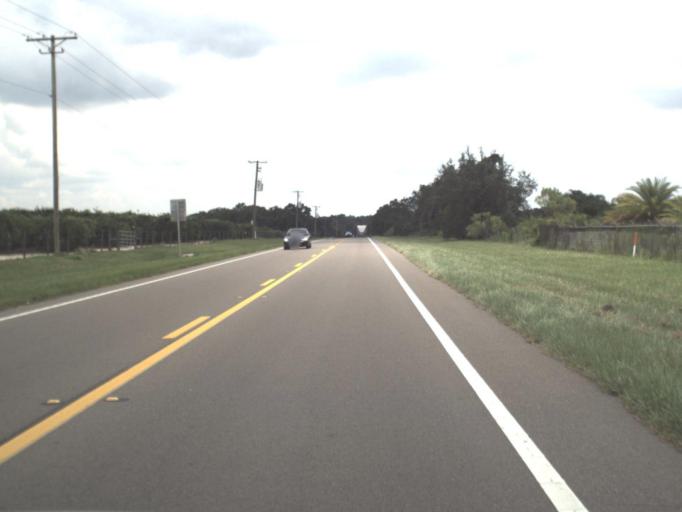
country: US
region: Florida
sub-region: Hillsborough County
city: Wimauma
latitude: 27.7090
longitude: -82.2666
